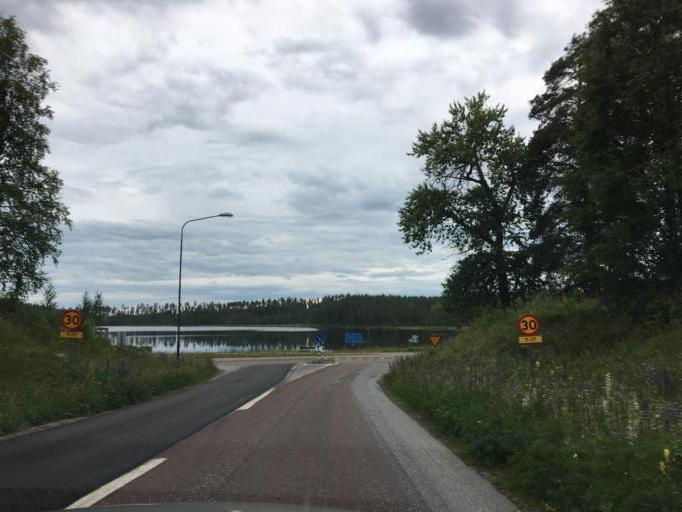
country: SE
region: Vaermland
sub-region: Filipstads Kommun
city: Lesjofors
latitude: 60.1389
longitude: 14.3853
